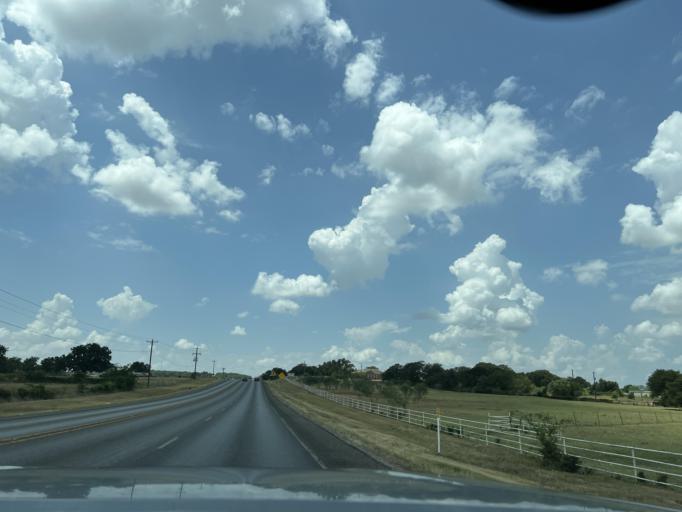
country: US
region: Texas
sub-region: Parker County
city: Springtown
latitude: 32.9459
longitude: -97.6917
